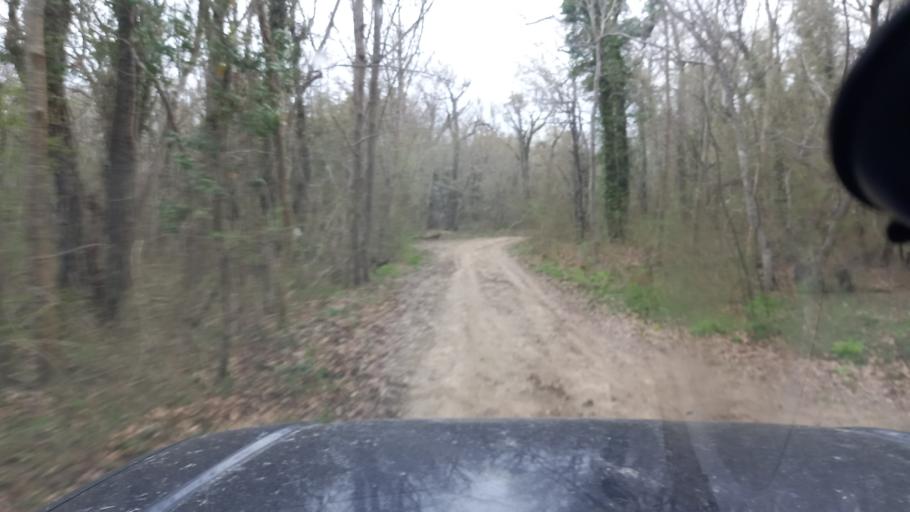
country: RU
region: Krasnodarskiy
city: Dzhubga
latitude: 44.3137
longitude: 38.6795
